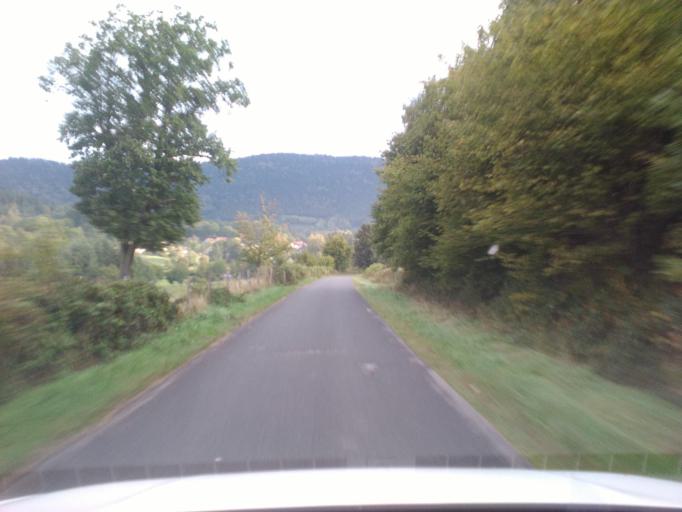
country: FR
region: Lorraine
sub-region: Departement des Vosges
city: Senones
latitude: 48.4080
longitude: 7.0376
